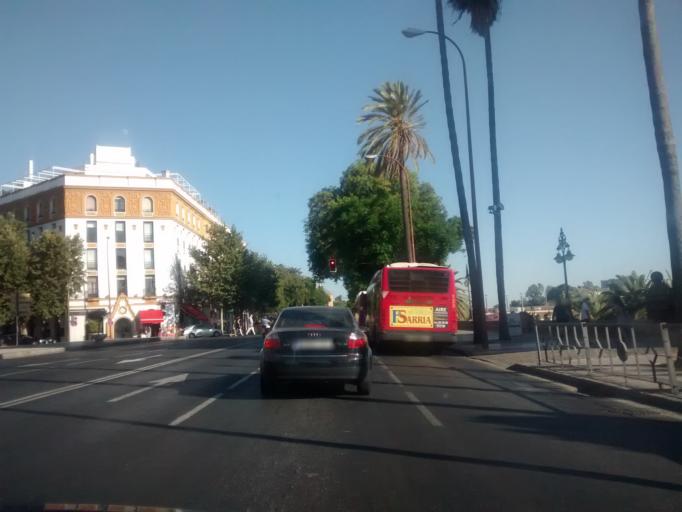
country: ES
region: Andalusia
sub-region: Provincia de Sevilla
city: Sevilla
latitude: 37.3827
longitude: -5.9962
